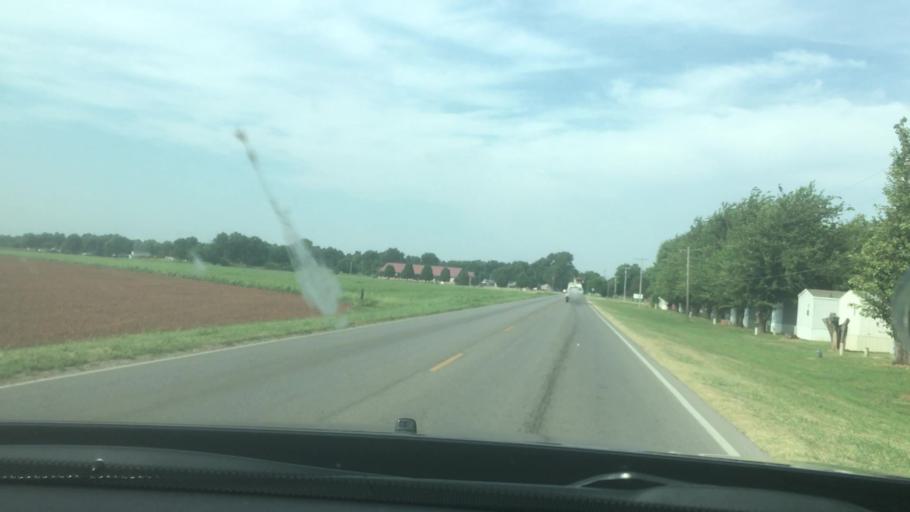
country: US
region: Oklahoma
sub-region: Garvin County
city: Pauls Valley
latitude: 34.7526
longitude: -97.2067
